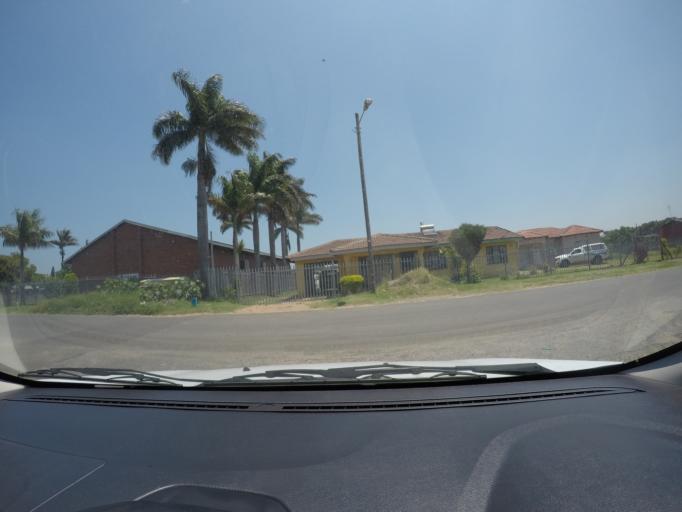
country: ZA
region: KwaZulu-Natal
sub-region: uThungulu District Municipality
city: eSikhawini
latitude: -28.8855
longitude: 31.8869
